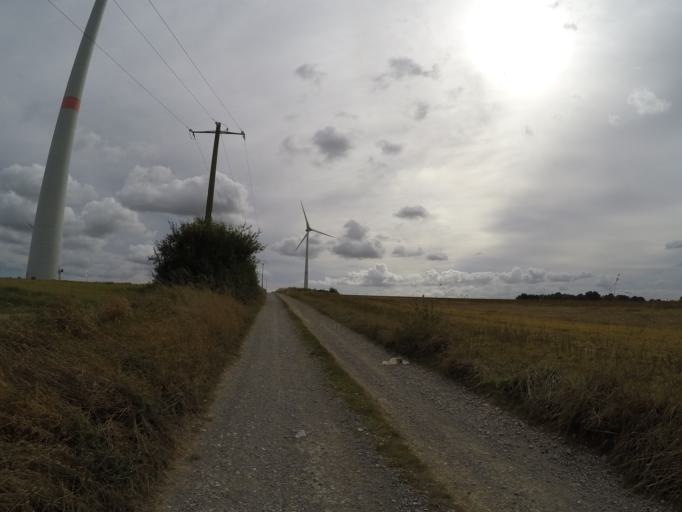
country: BE
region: Wallonia
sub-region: Province de Namur
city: Assesse
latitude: 50.2987
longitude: 4.9822
